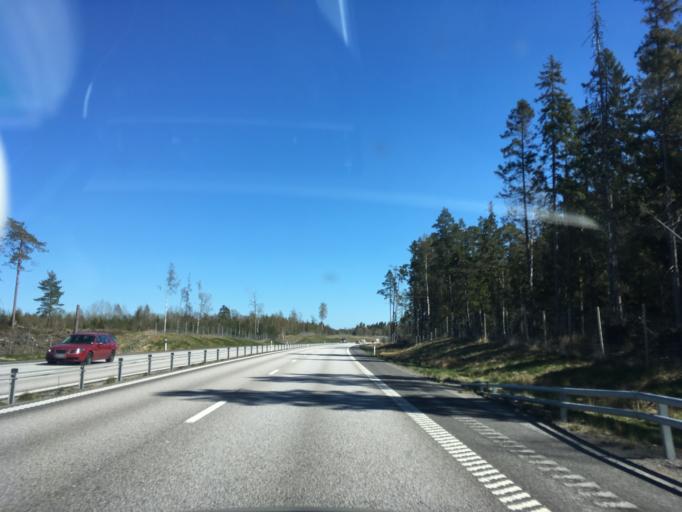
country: SE
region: Vaestra Goetaland
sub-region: Trollhattan
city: Sjuntorp
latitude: 58.2328
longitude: 12.2235
